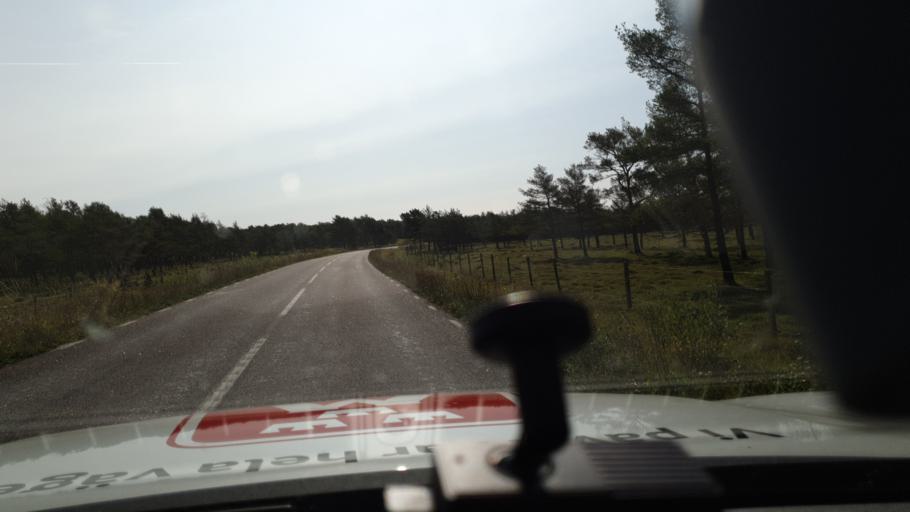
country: SE
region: Gotland
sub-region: Gotland
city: Hemse
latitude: 57.1026
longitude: 18.3011
